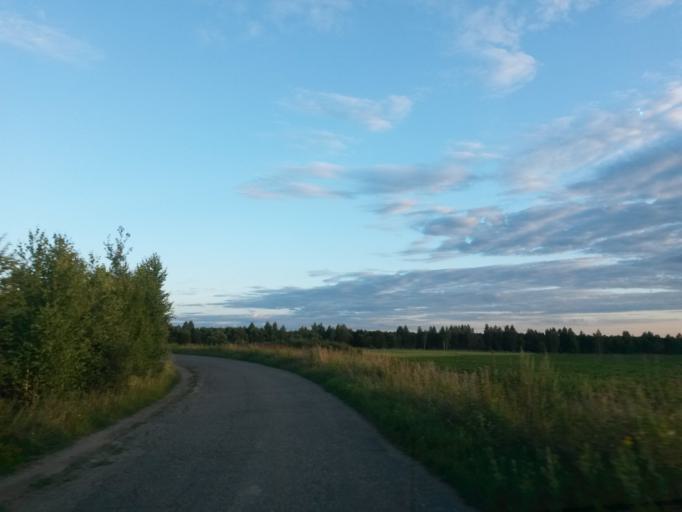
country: RU
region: Jaroslavl
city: Gavrilov-Yam
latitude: 57.3386
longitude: 40.0369
